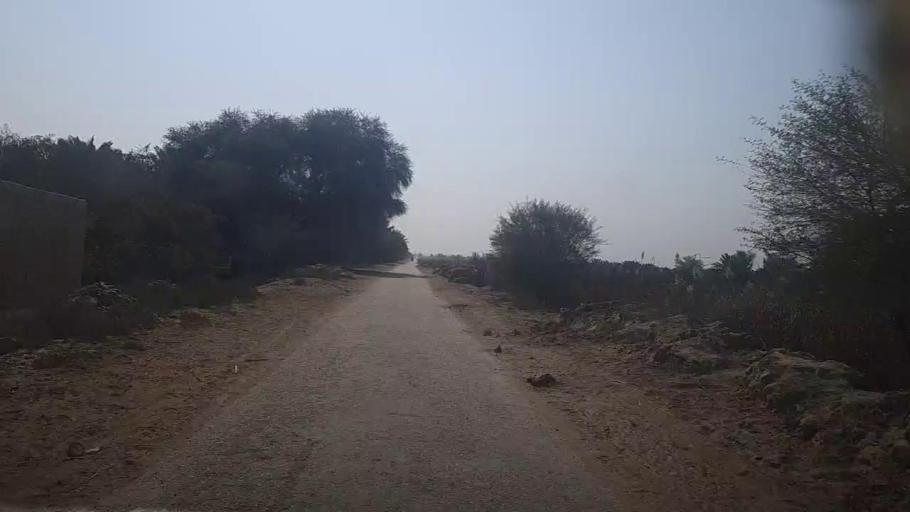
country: PK
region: Sindh
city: Khairpur
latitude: 27.4511
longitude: 68.8120
